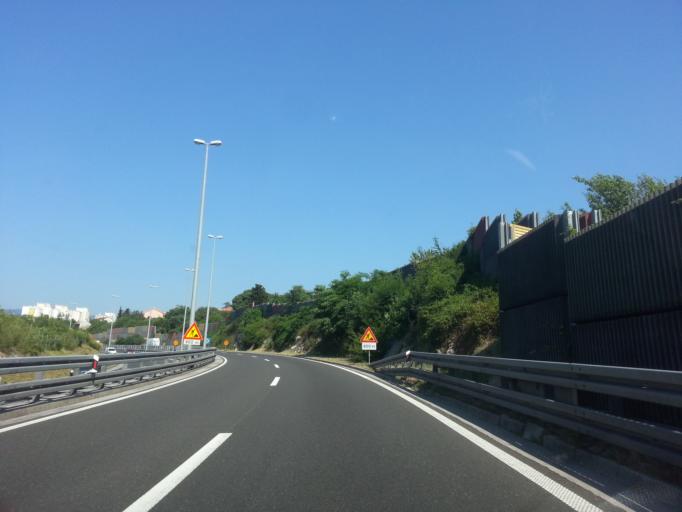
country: HR
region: Primorsko-Goranska
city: Drenova
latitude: 45.3365
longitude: 14.4432
